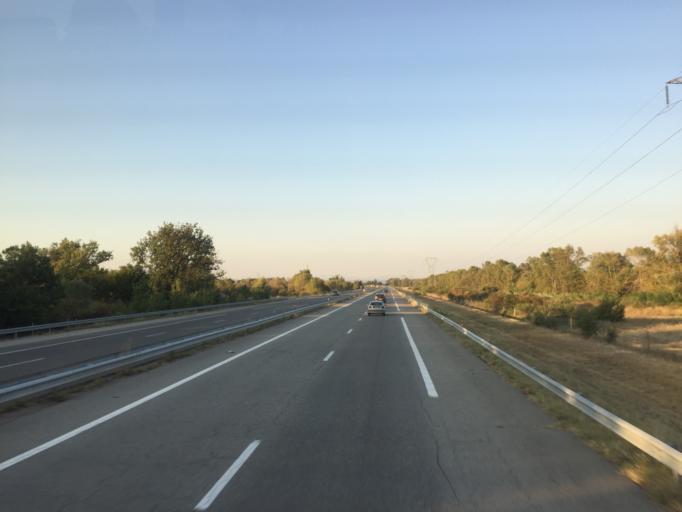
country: FR
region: Provence-Alpes-Cote d'Azur
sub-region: Departement des Alpes-de-Haute-Provence
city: Sainte-Tulle
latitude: 43.7508
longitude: 5.7674
